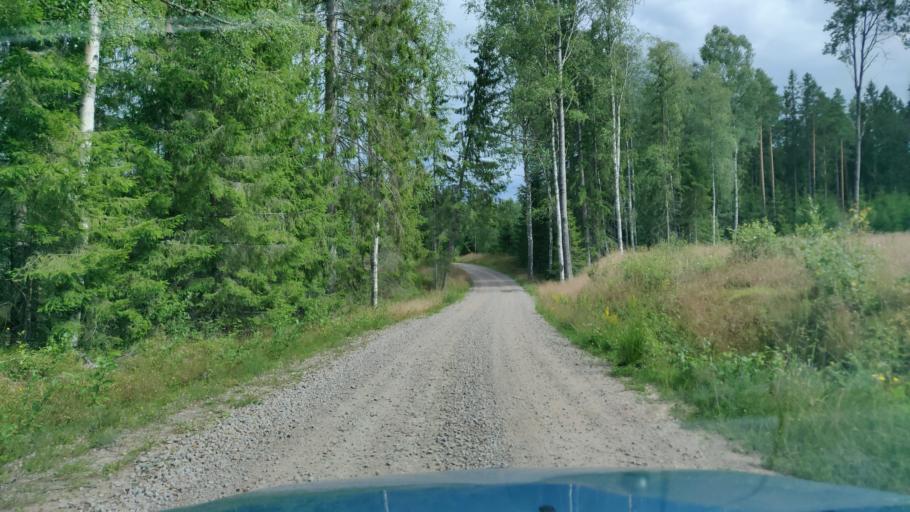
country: SE
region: Vaermland
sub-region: Munkfors Kommun
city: Munkfors
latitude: 59.9406
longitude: 13.5857
